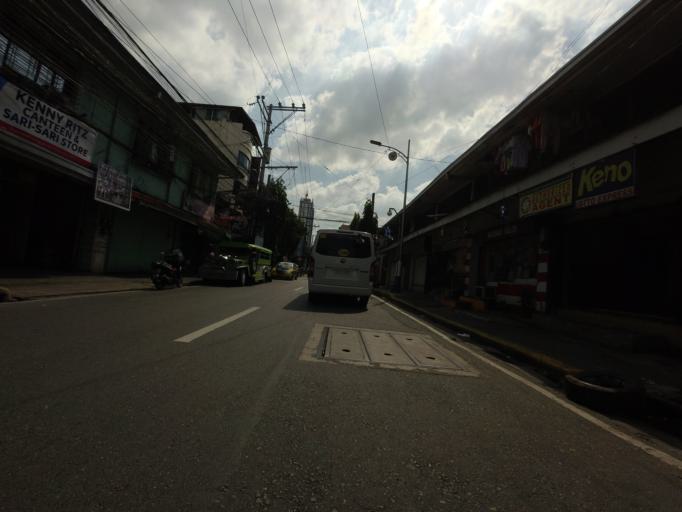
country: PH
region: Metro Manila
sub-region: City of Manila
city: Port Area
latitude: 14.5679
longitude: 120.9963
